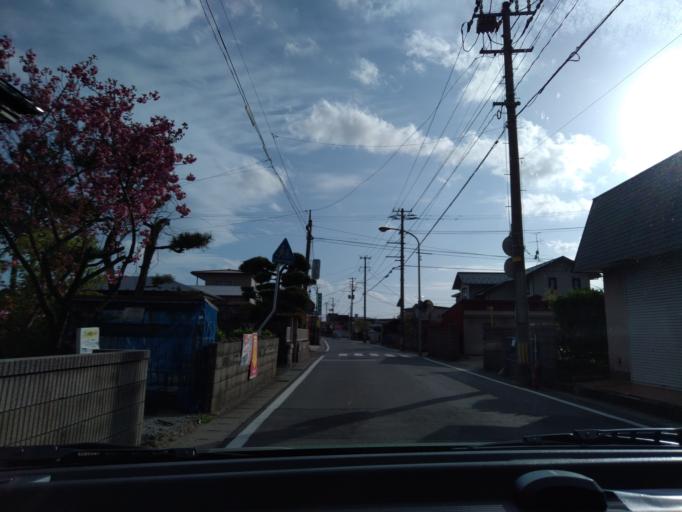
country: JP
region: Akita
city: Akita Shi
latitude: 39.7669
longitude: 140.0787
